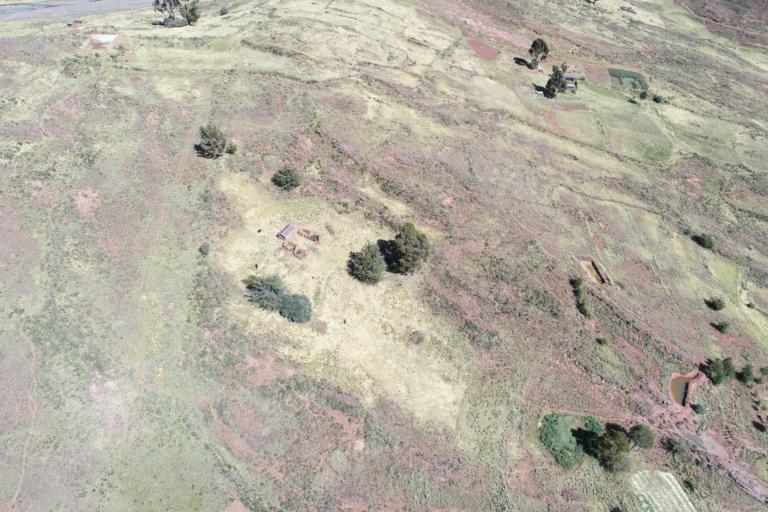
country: BO
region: La Paz
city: Tiahuanaco
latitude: -16.6082
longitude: -68.7630
